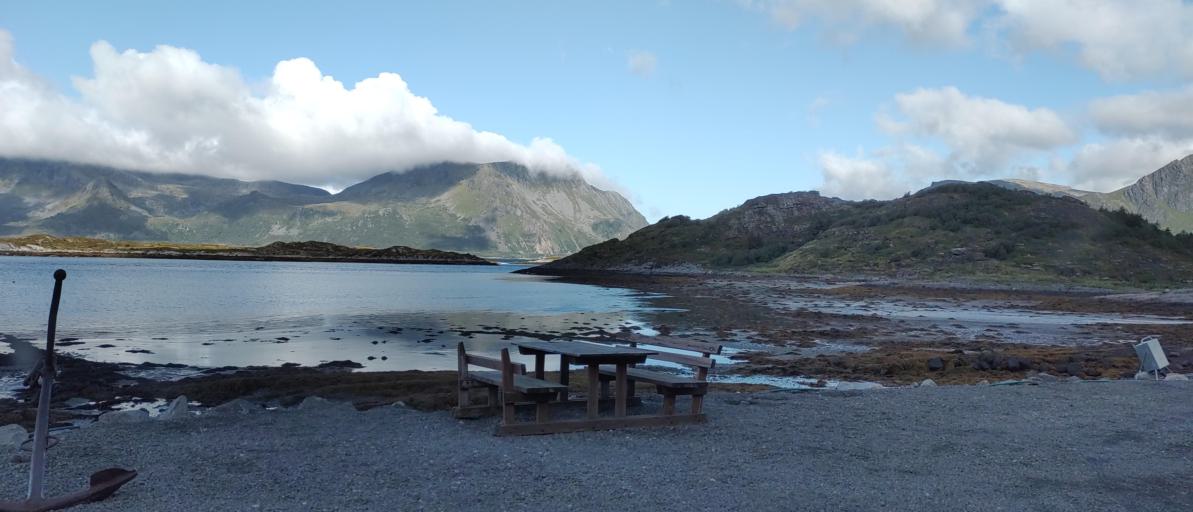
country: NO
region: Nordland
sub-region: Vagan
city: Kabelvag
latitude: 68.2244
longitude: 14.2162
